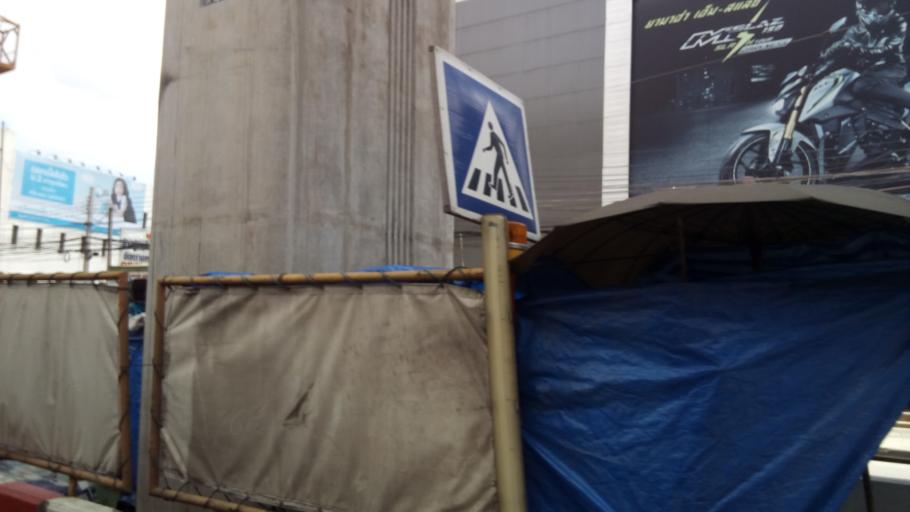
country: TH
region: Bangkok
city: Bang Khen
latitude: 13.8894
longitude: 100.6048
